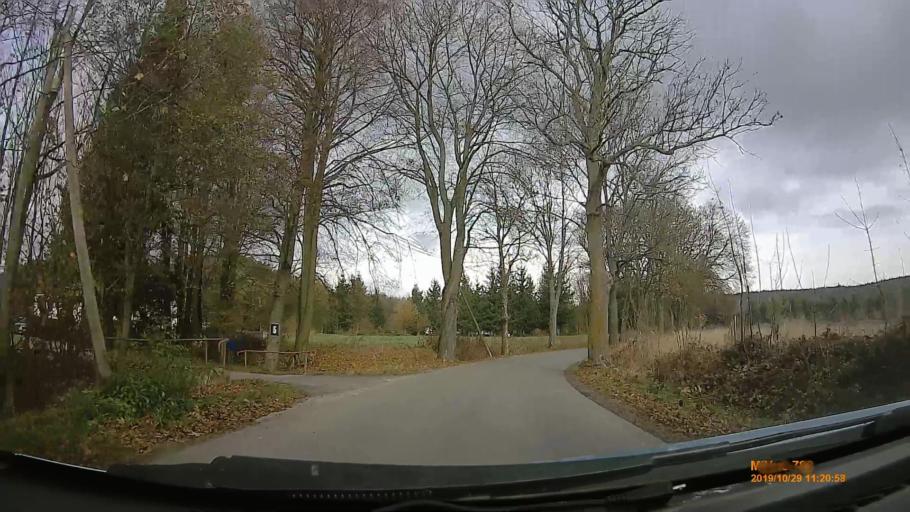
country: PL
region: Lower Silesian Voivodeship
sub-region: Powiat klodzki
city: Szczytna
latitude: 50.4254
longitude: 16.4383
